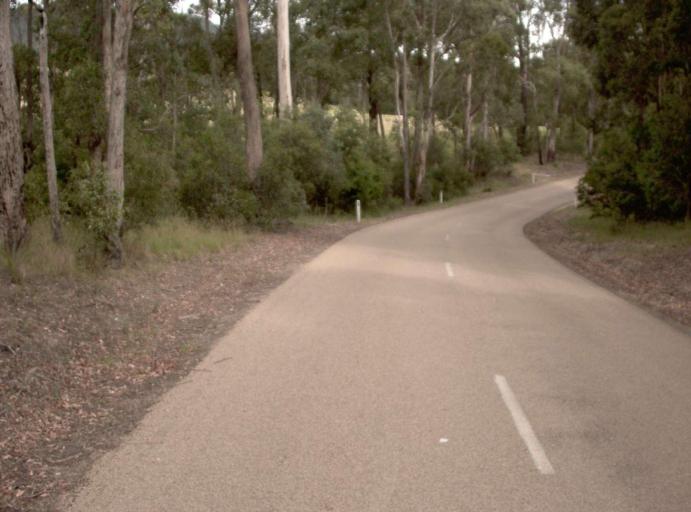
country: AU
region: Victoria
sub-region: East Gippsland
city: Bairnsdale
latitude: -37.7156
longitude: 147.5925
